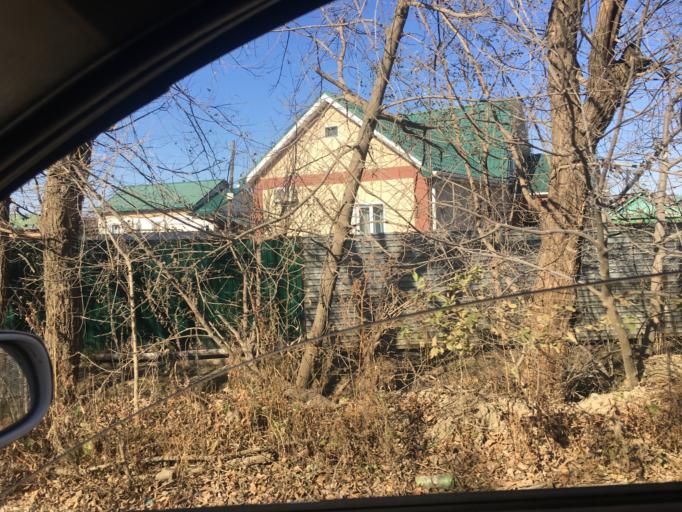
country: RU
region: Primorskiy
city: Dal'nerechensk
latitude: 45.9310
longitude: 133.7105
